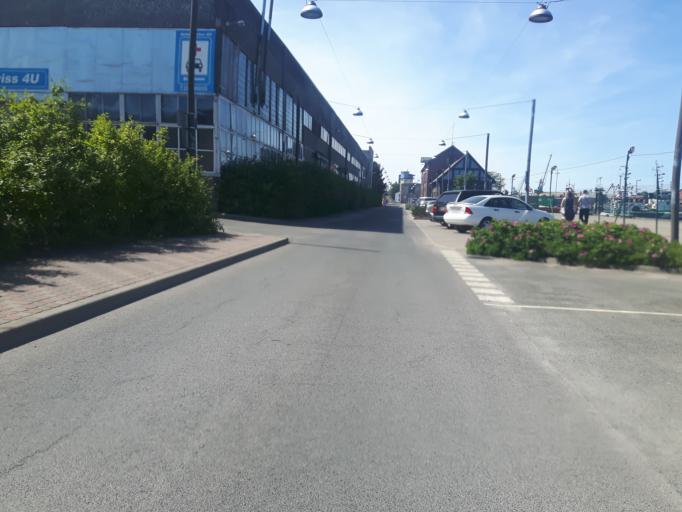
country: LV
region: Liepaja
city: Liepaja
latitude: 56.5137
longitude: 21.0058
